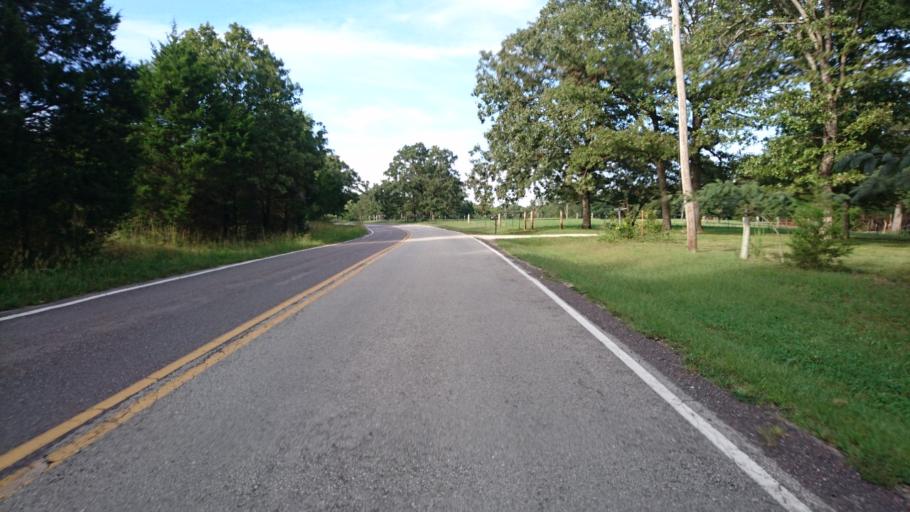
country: US
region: Missouri
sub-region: Crawford County
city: Cuba
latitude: 38.1003
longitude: -91.3630
